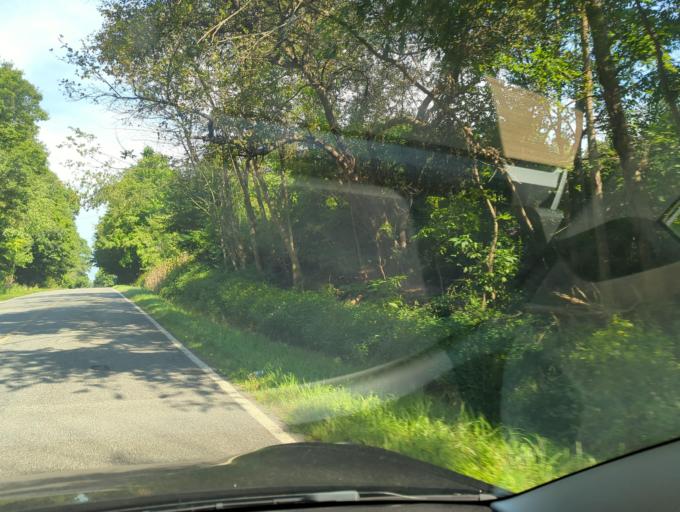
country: US
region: Michigan
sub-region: Ionia County
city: Ionia
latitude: 42.9296
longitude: -85.1204
